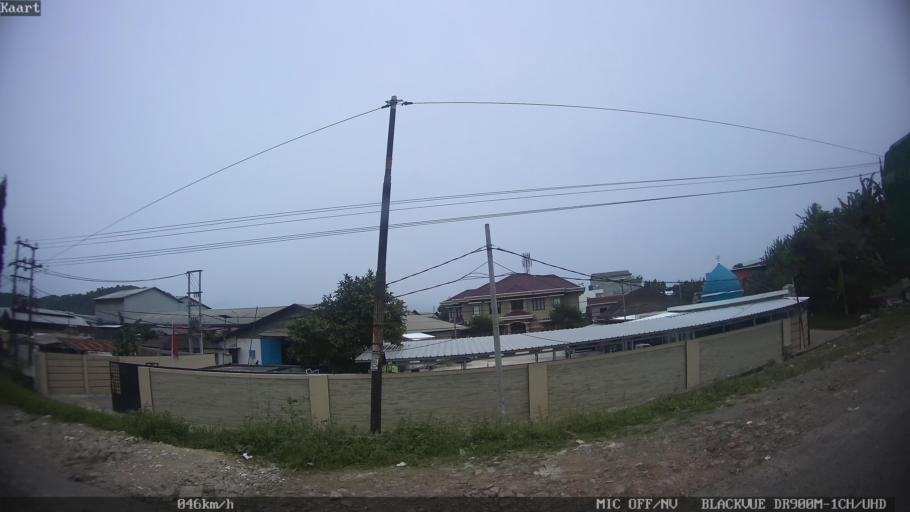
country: ID
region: Lampung
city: Bandarlampung
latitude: -5.4180
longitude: 105.2956
